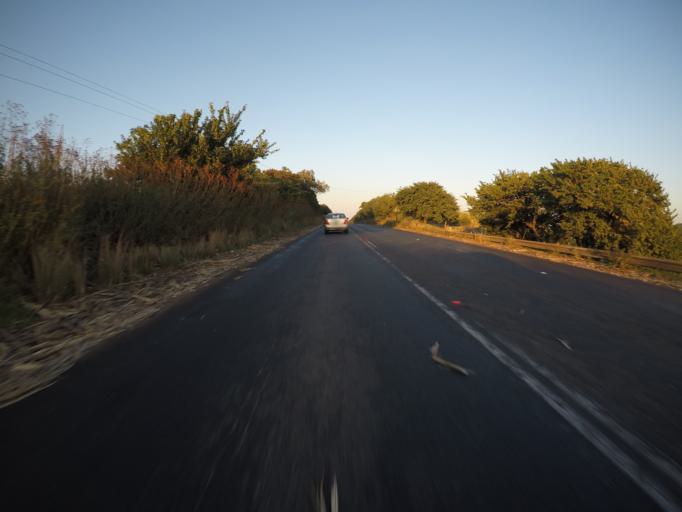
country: ZA
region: KwaZulu-Natal
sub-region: uThungulu District Municipality
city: Empangeni
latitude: -28.8162
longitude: 31.8876
